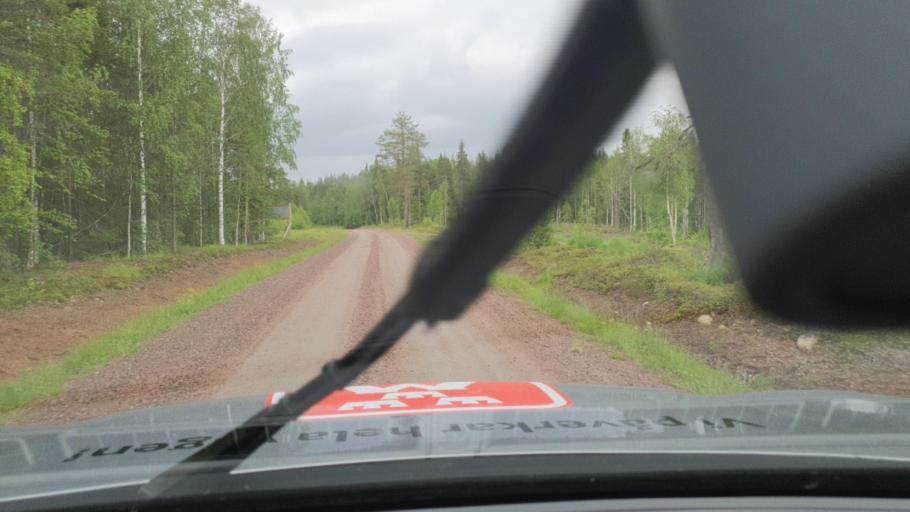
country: SE
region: Norrbotten
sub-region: Overkalix Kommun
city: OEverkalix
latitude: 66.6241
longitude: 22.7247
